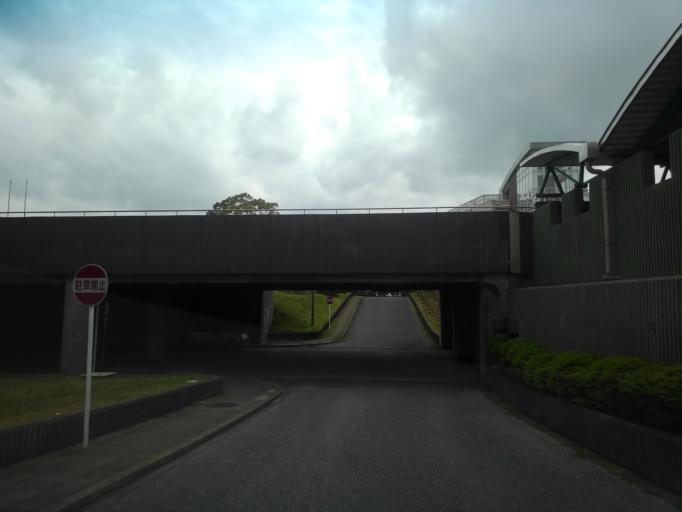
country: JP
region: Chiba
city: Kimitsu
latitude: 35.3306
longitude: 139.9019
